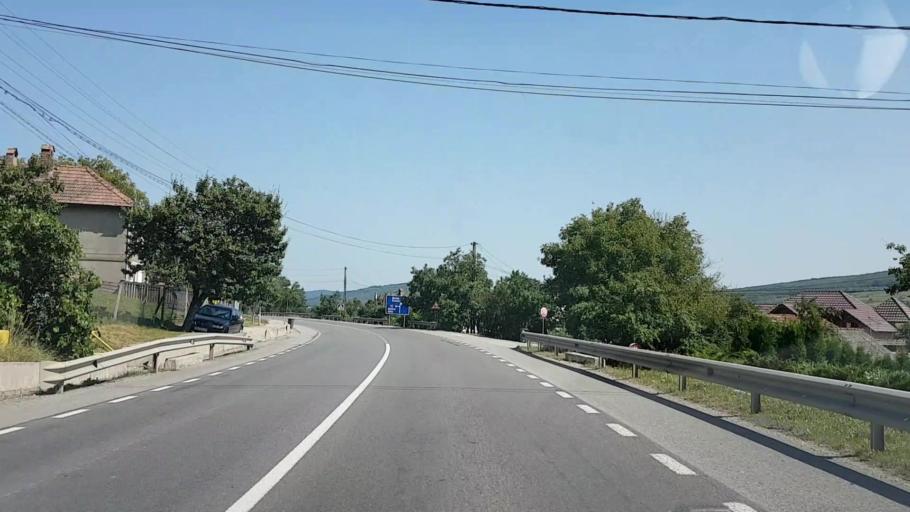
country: RO
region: Bistrita-Nasaud
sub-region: Comuna Beclean
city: Beclean
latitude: 47.1804
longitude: 24.1404
